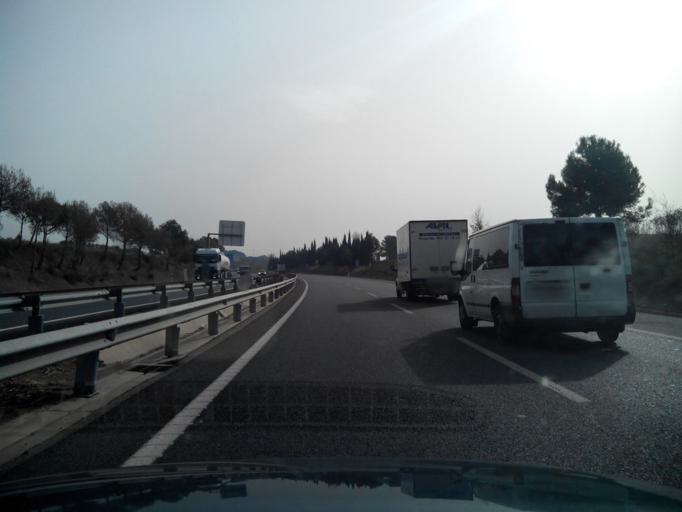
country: ES
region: Catalonia
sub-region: Provincia de Tarragona
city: Reus
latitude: 41.1308
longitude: 1.1090
